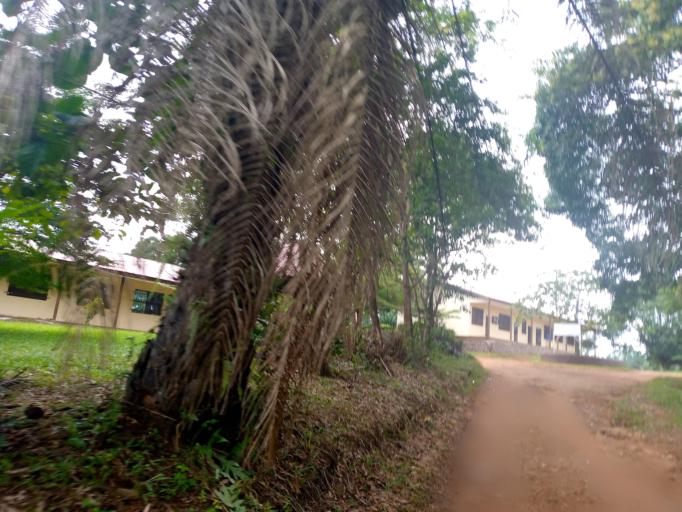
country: SL
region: Eastern Province
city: Kenema
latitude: 7.8650
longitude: -11.1830
